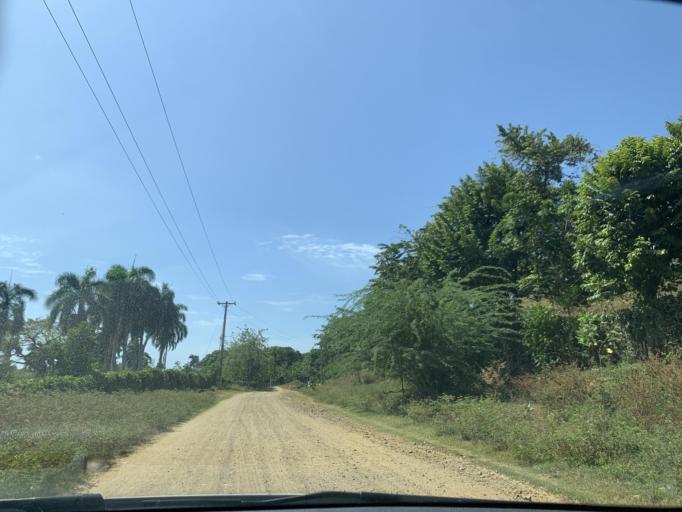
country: DO
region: Puerto Plata
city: Luperon
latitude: 19.8850
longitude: -70.8730
